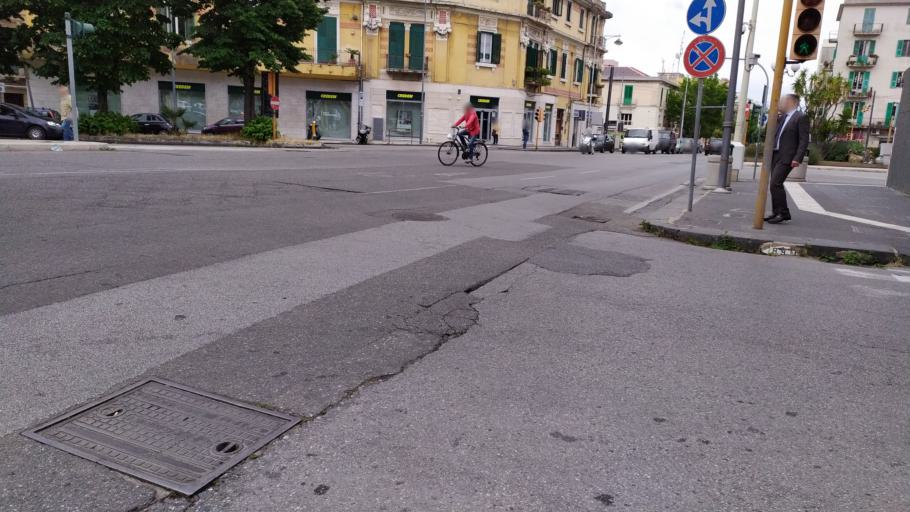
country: IT
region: Sicily
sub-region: Messina
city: Messina
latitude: 38.1869
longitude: 15.5558
